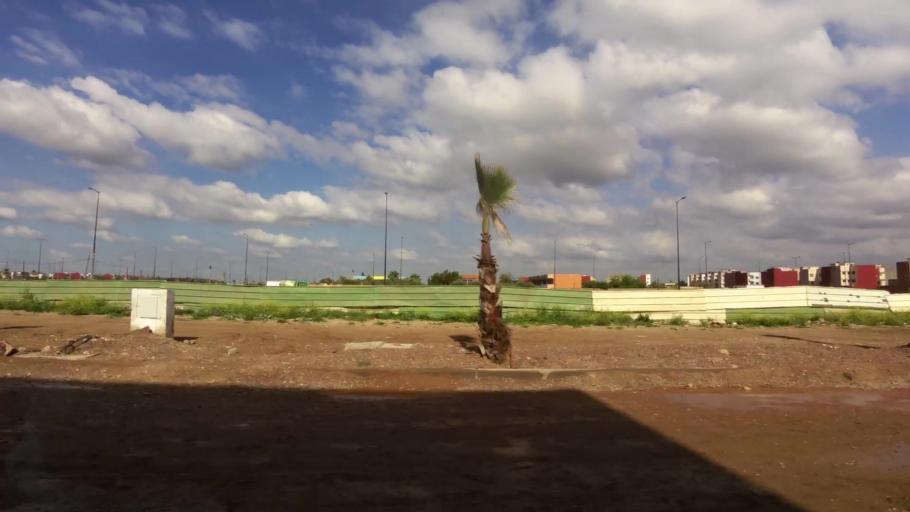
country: MA
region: Chaouia-Ouardigha
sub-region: Settat Province
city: Berrechid
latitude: 33.2651
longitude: -7.5714
